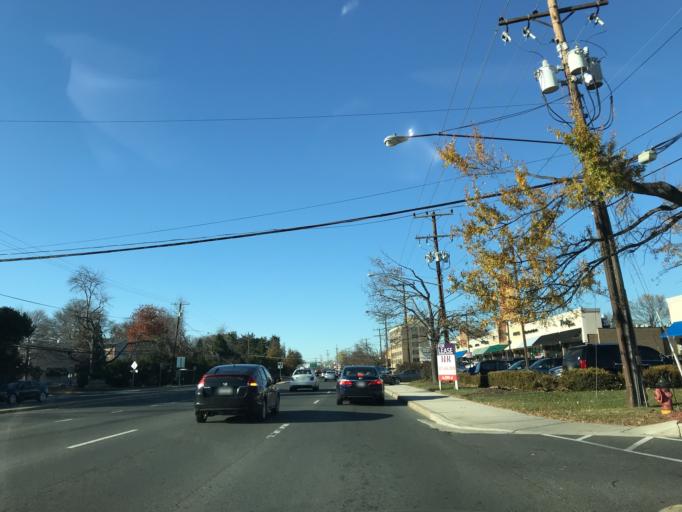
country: US
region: Maryland
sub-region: Montgomery County
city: Rockville
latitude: 39.0718
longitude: -77.1327
